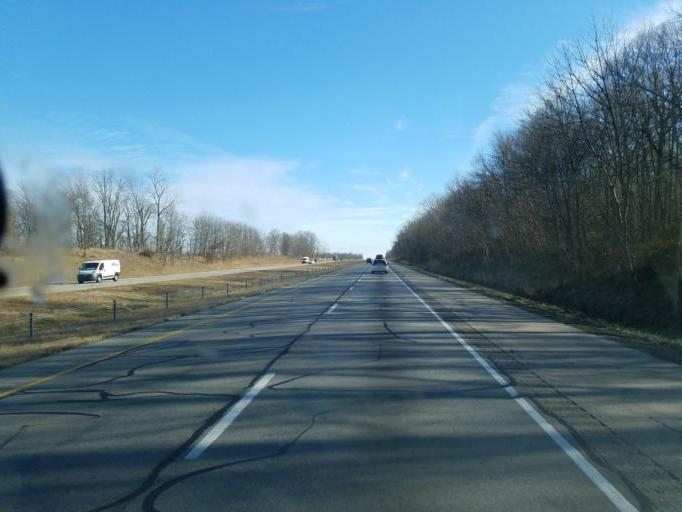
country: US
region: Indiana
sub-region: Henry County
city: New Castle
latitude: 39.8529
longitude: -85.3451
